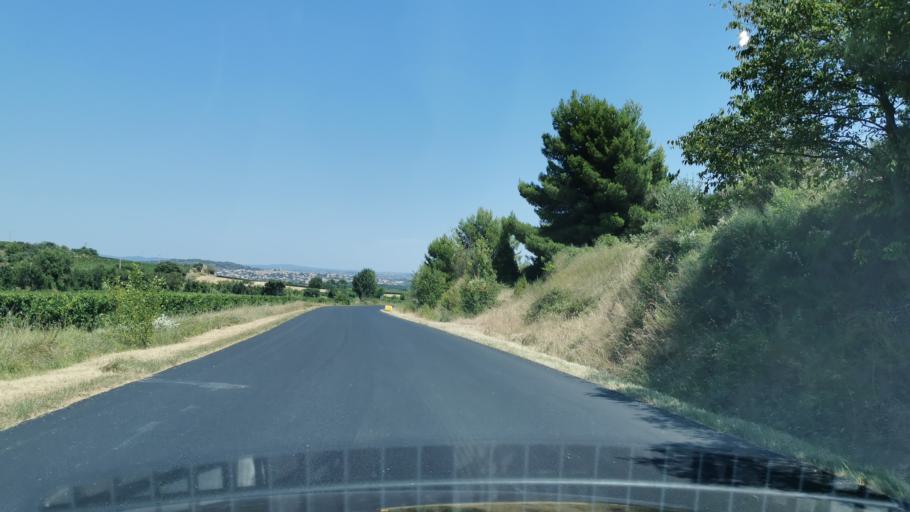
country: FR
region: Languedoc-Roussillon
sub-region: Departement de l'Herault
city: Cazouls-les-Beziers
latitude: 43.4061
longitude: 3.1086
